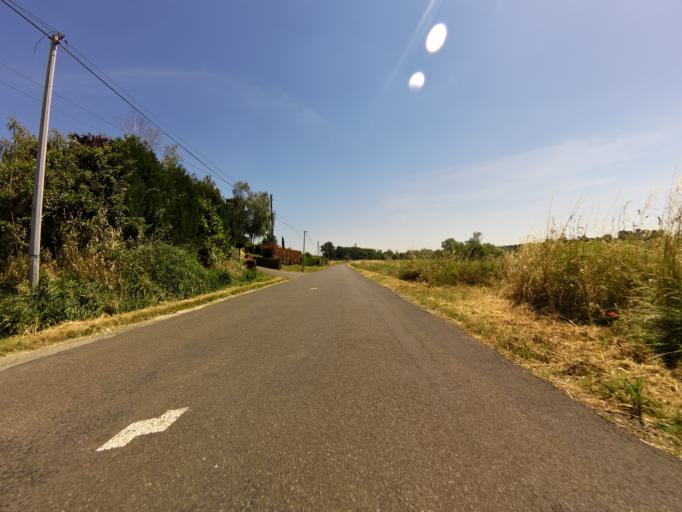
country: FR
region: Pays de la Loire
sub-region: Departement de la Loire-Atlantique
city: Le Loroux-Bottereau
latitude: 47.2057
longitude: -1.3808
